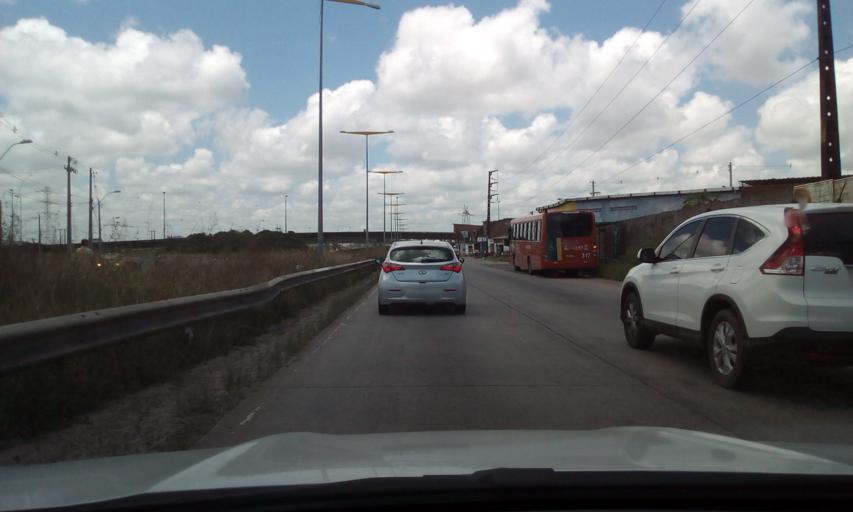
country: BR
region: Pernambuco
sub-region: Recife
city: Recife
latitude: -8.0705
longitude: -34.9396
